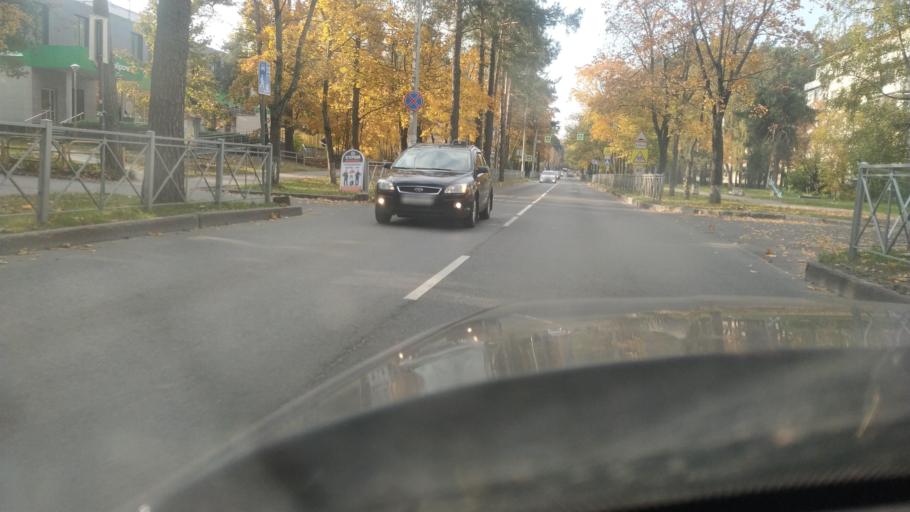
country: RU
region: Leningrad
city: Sosnovyy Bor
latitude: 59.8910
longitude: 29.0926
